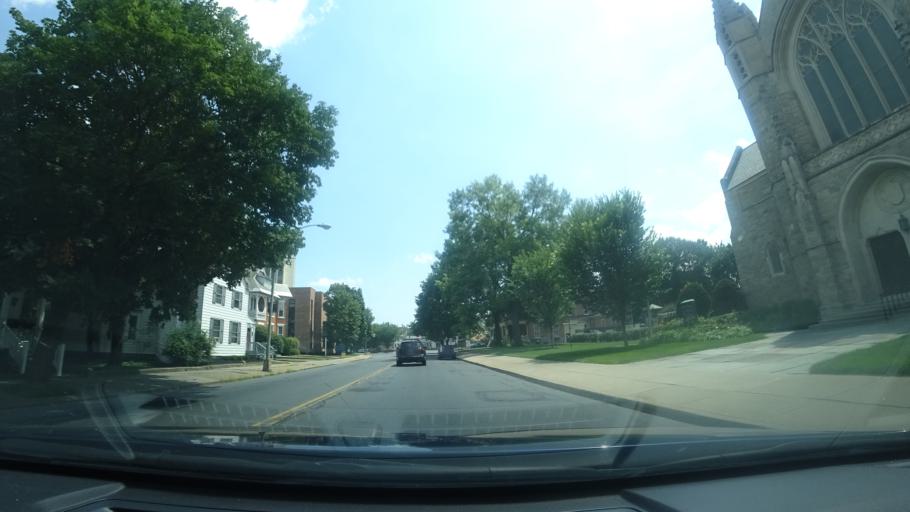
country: US
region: New York
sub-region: Warren County
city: Glens Falls
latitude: 43.3129
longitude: -73.6507
